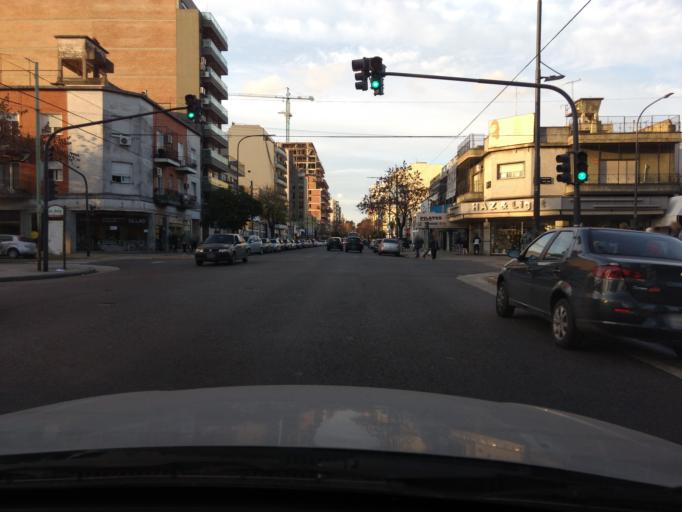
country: AR
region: Buenos Aires F.D.
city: Villa Santa Rita
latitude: -34.6099
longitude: -58.5183
